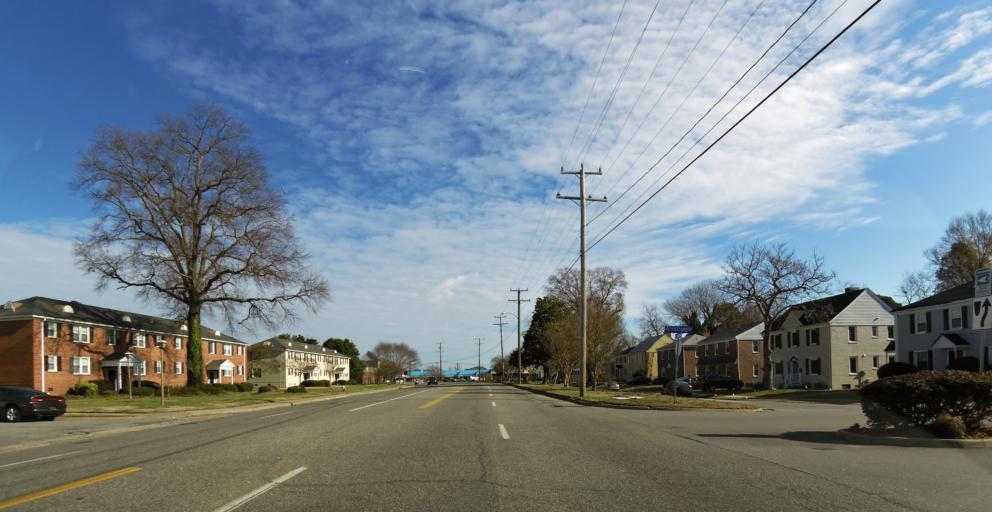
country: US
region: Virginia
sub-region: City of Hampton
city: Hampton
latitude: 37.0094
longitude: -76.3554
